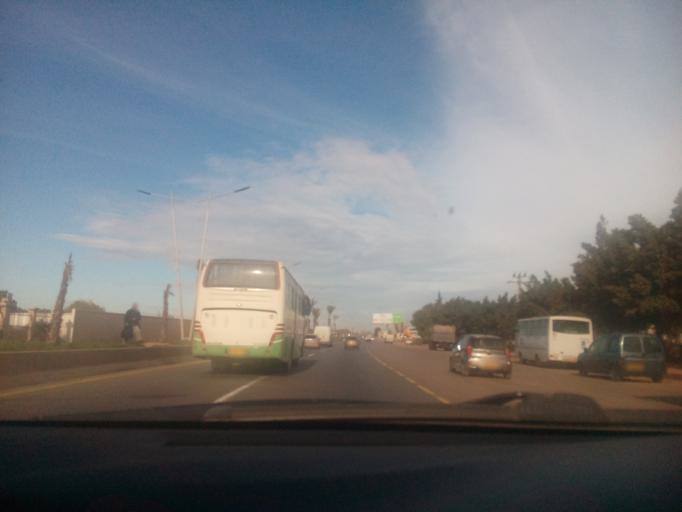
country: DZ
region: Oran
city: Es Senia
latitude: 35.6162
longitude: -0.5839
